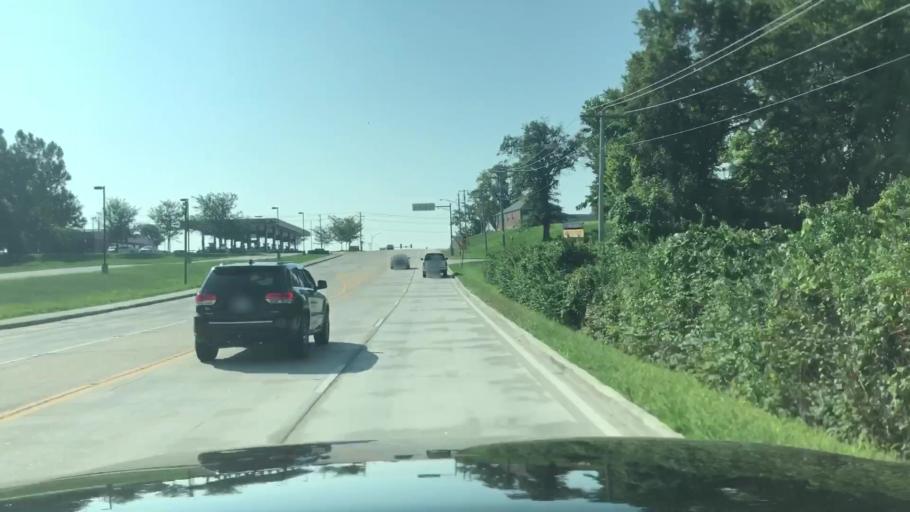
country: US
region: Missouri
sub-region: Saint Charles County
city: Saint Charles
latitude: 38.7710
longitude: -90.5260
